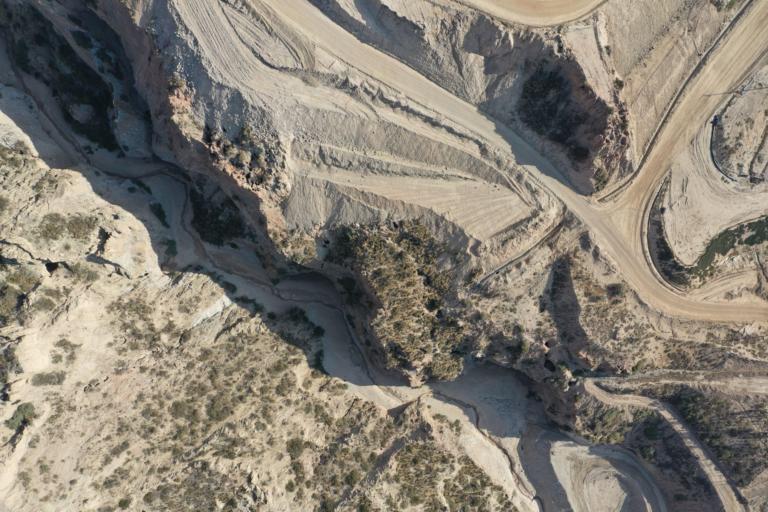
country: BO
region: La Paz
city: La Paz
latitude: -16.5596
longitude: -68.1291
